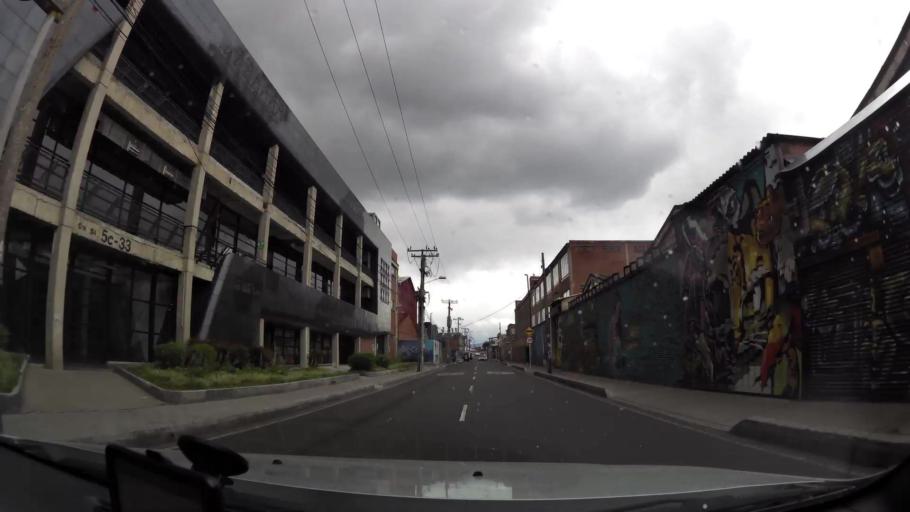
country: CO
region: Bogota D.C.
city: Bogota
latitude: 4.6255
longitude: -74.1136
